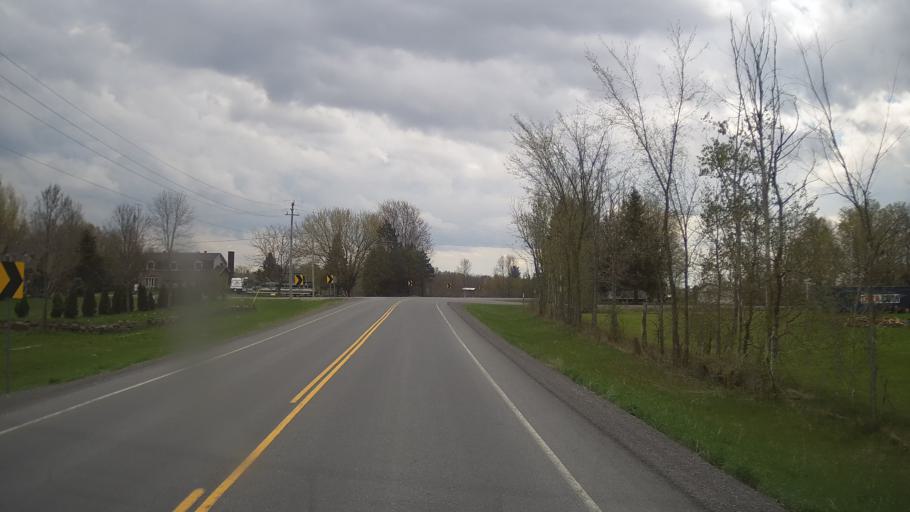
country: CA
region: Ontario
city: Hawkesbury
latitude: 45.5663
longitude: -74.5264
